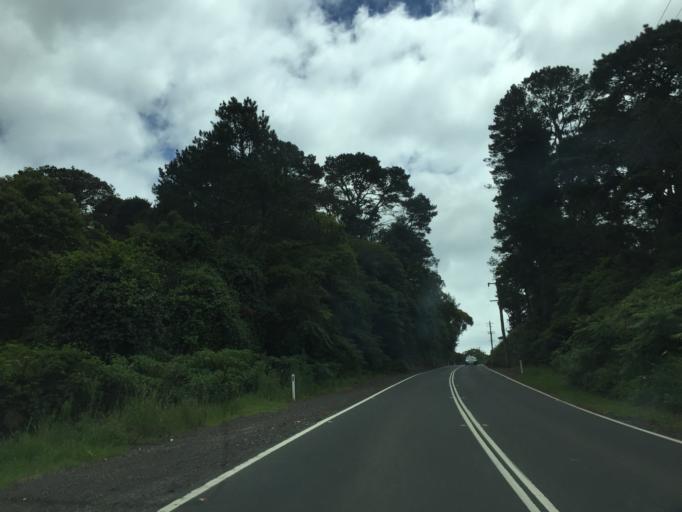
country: AU
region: New South Wales
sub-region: Hawkesbury
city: Richmond
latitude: -33.5223
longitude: 150.6279
